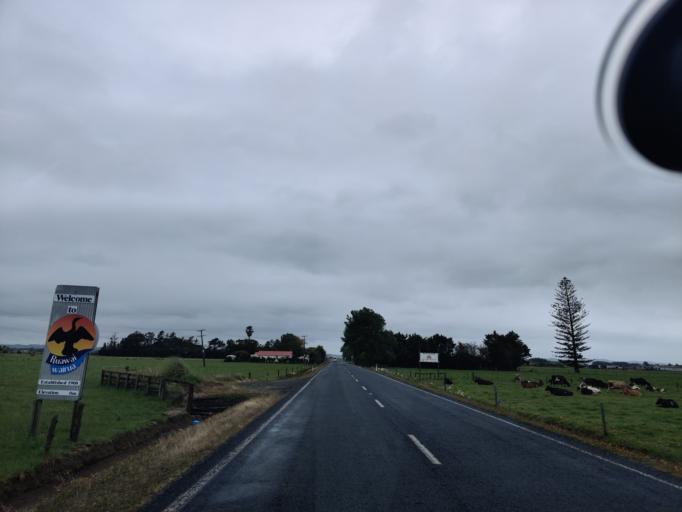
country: NZ
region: Northland
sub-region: Kaipara District
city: Dargaville
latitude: -36.1219
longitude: 174.0051
